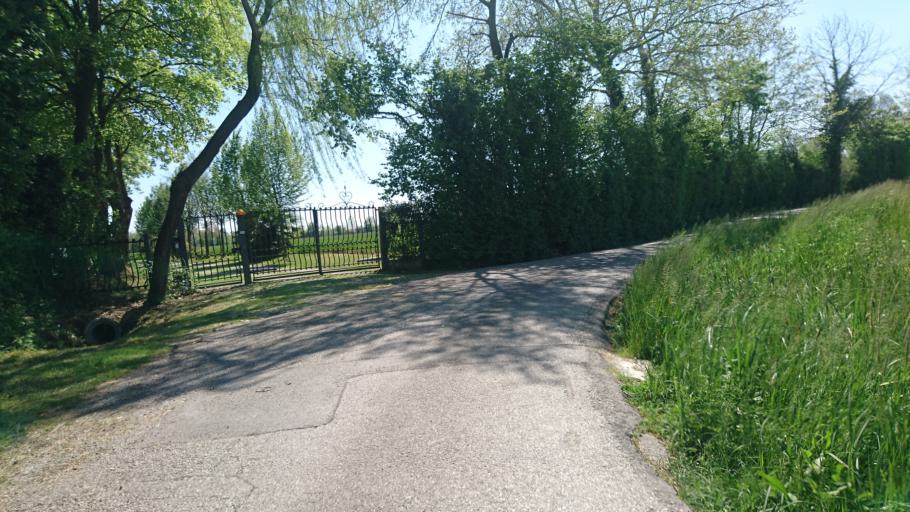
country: IT
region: Veneto
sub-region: Provincia di Treviso
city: Conscio
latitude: 45.6157
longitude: 12.2742
